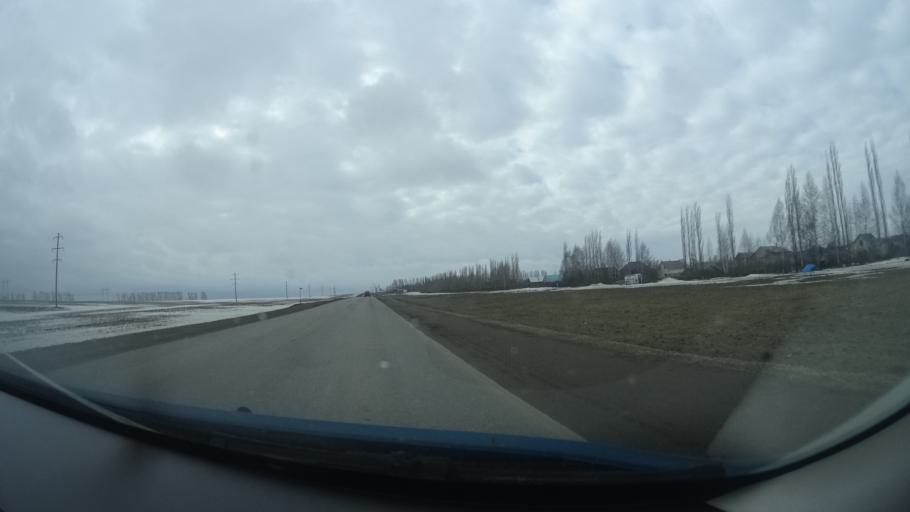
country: RU
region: Bashkortostan
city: Birsk
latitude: 55.4378
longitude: 55.5873
